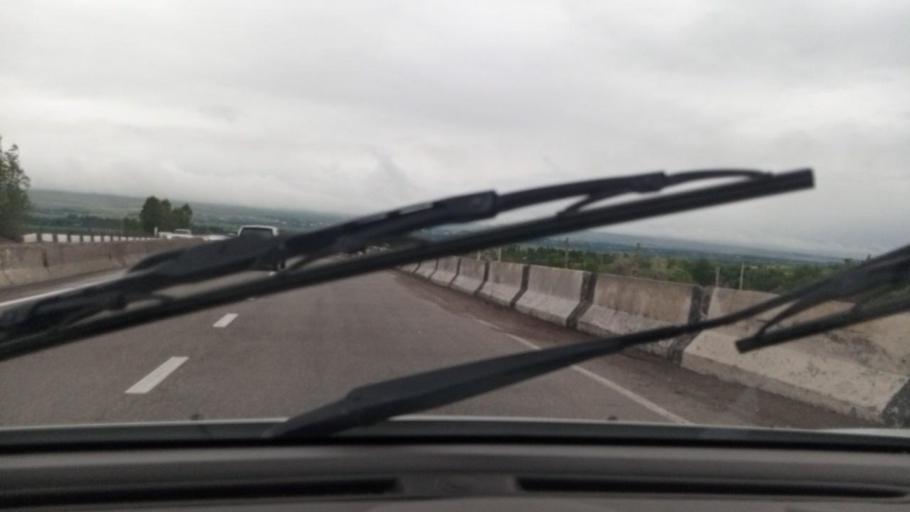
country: UZ
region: Toshkent
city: Angren
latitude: 40.9453
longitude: 69.9072
